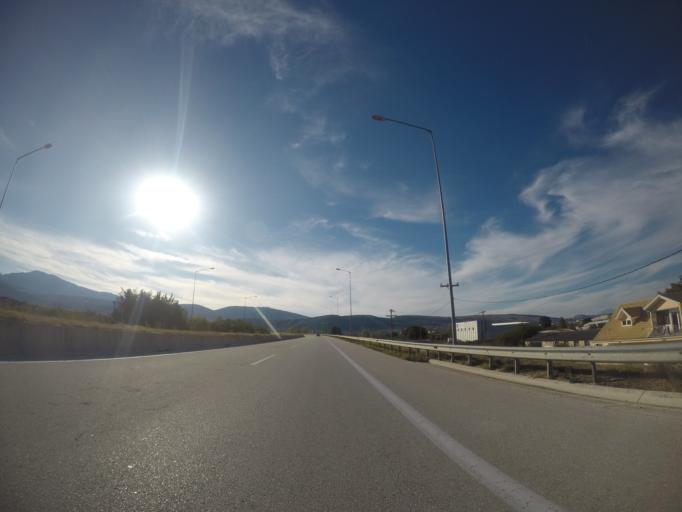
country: GR
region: Epirus
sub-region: Nomos Ioanninon
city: Katsikas
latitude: 39.6038
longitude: 20.8761
